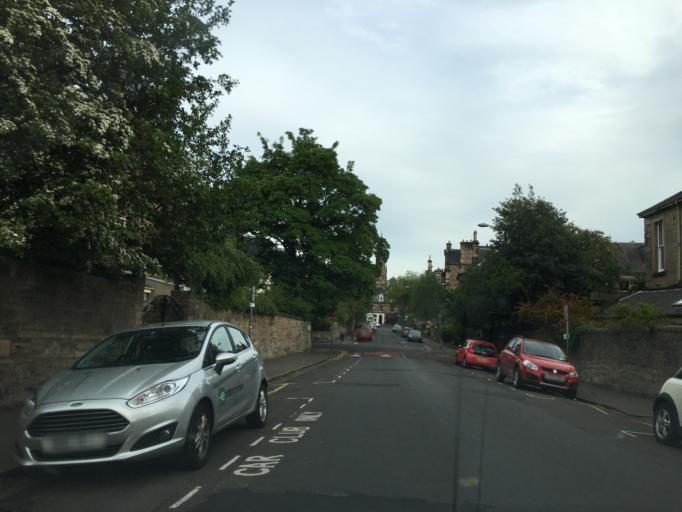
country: GB
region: Scotland
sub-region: Edinburgh
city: Edinburgh
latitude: 55.9354
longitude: -3.2132
